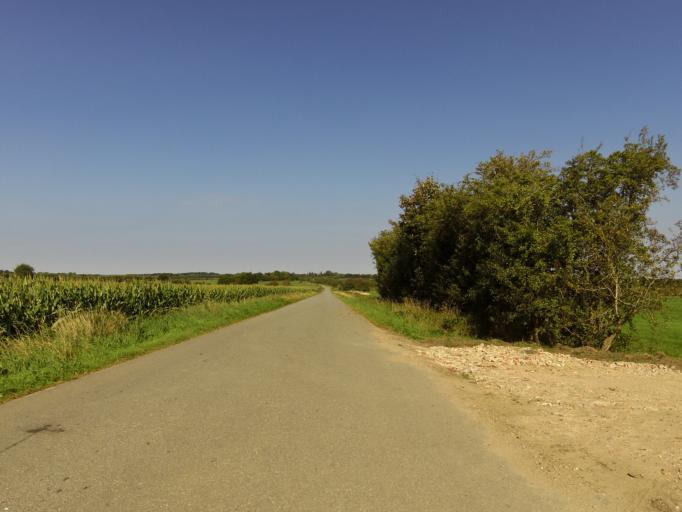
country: DK
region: South Denmark
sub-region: Vejen Kommune
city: Rodding
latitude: 55.3607
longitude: 9.1281
